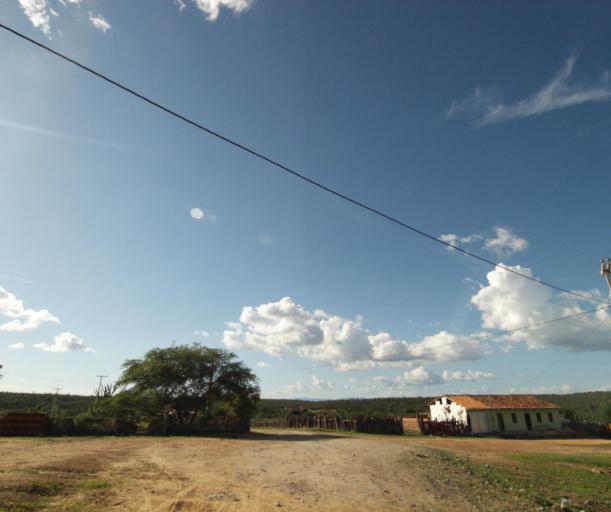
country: BR
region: Bahia
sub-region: Tanhacu
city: Tanhacu
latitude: -14.1831
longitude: -41.0125
